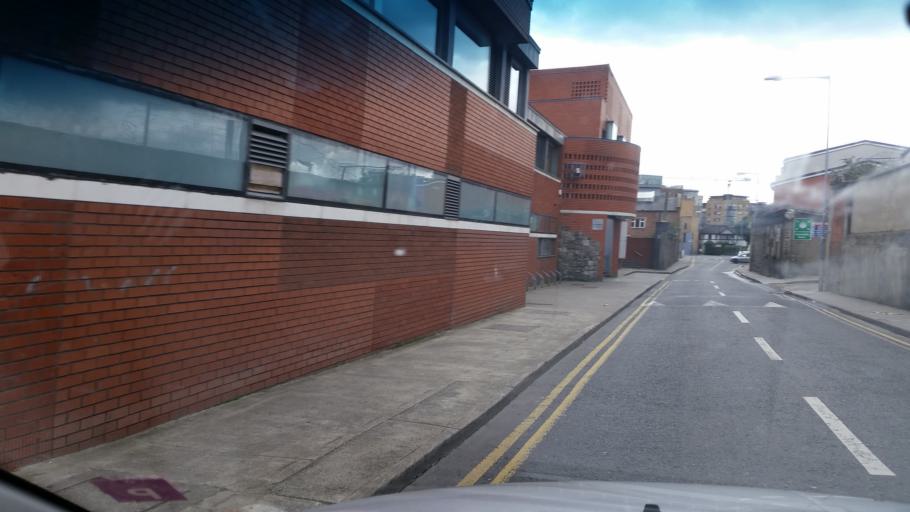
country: IE
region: Leinster
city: Rialto
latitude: 53.3394
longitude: -6.2867
